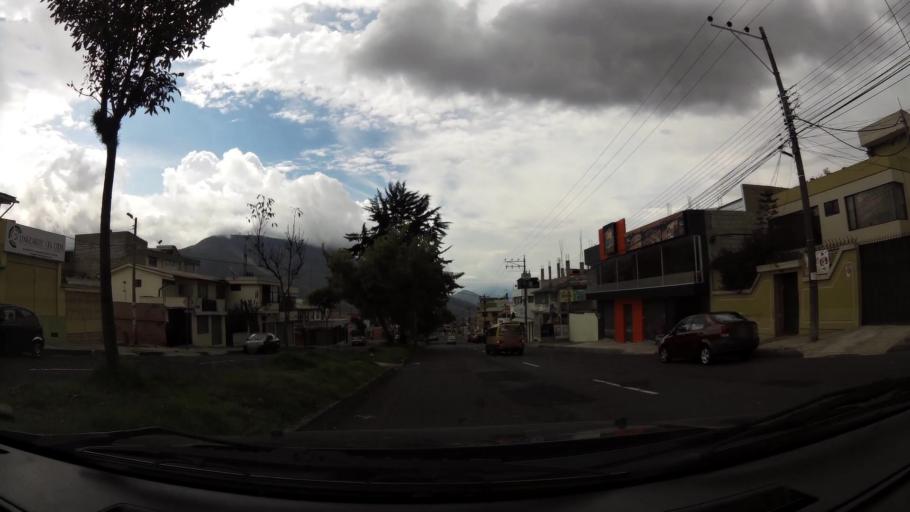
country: EC
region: Pichincha
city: Quito
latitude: -0.0864
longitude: -78.4672
